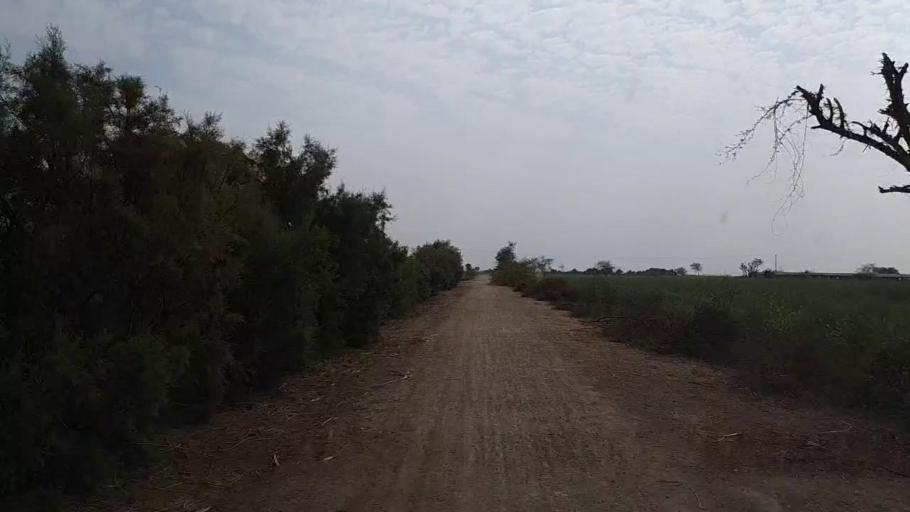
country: PK
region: Sindh
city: Mirwah Gorchani
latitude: 25.3944
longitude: 69.1018
